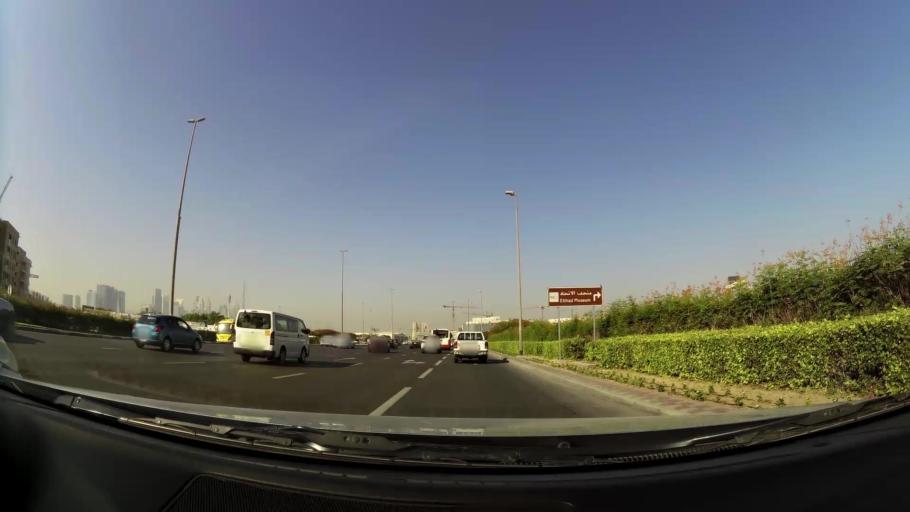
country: AE
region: Ash Shariqah
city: Sharjah
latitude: 25.2514
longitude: 55.2813
